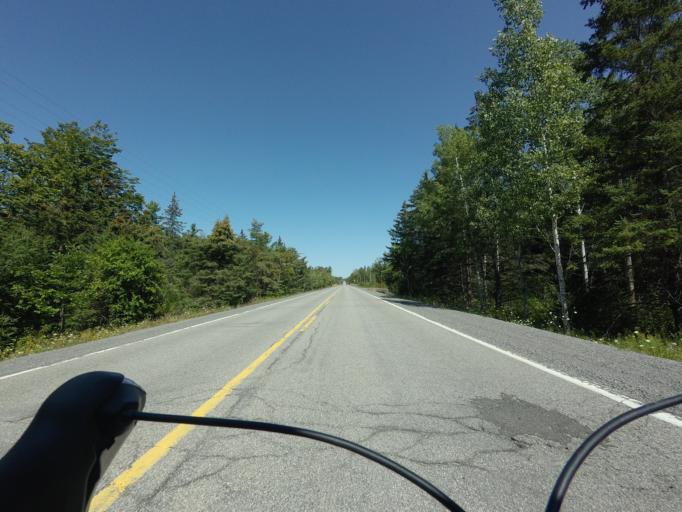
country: CA
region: Ontario
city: Bells Corners
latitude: 45.3896
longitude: -75.9370
